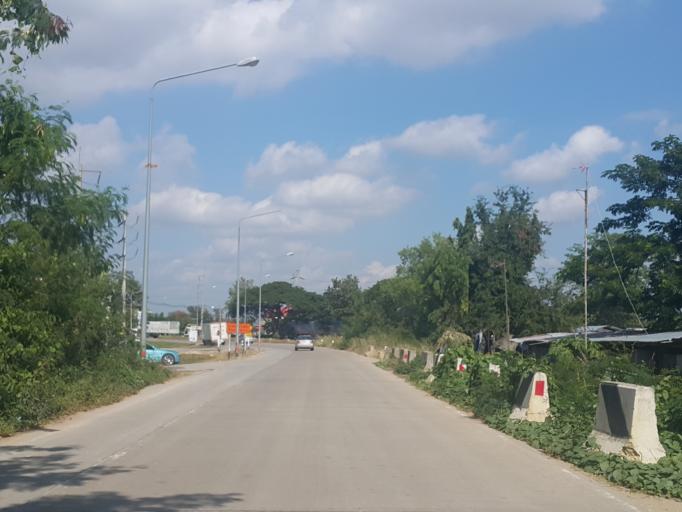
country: TH
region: Chiang Mai
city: Saraphi
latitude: 18.7366
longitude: 99.0355
